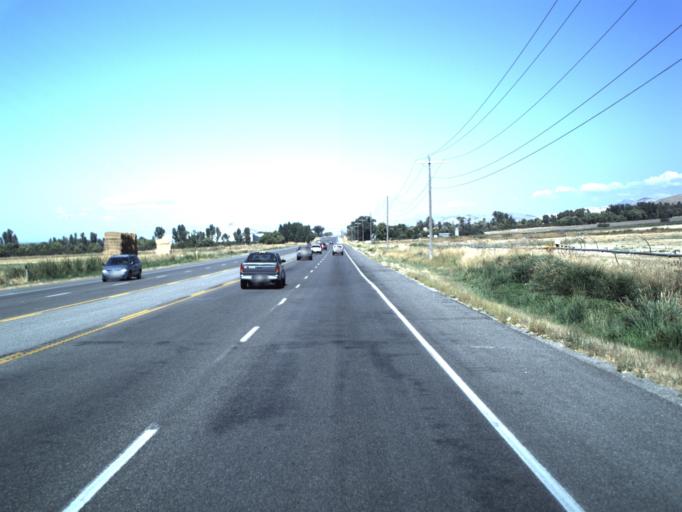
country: US
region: Utah
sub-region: Cache County
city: Richmond
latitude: 41.9291
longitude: -111.8141
